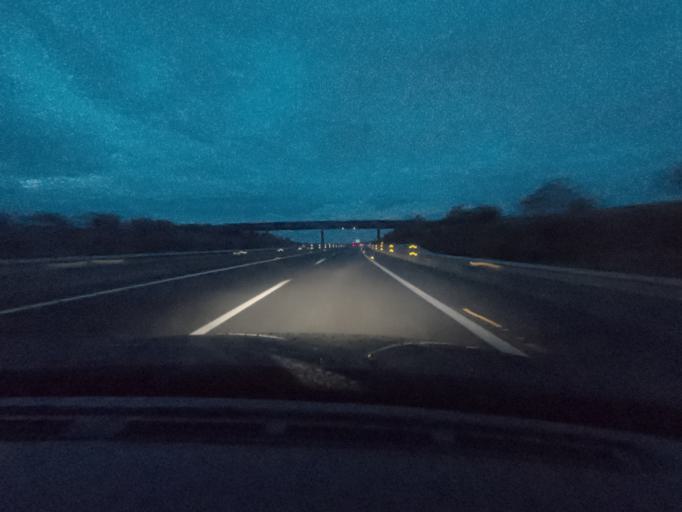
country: ES
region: Extremadura
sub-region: Provincia de Caceres
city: Caceres
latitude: 39.4137
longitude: -6.4020
